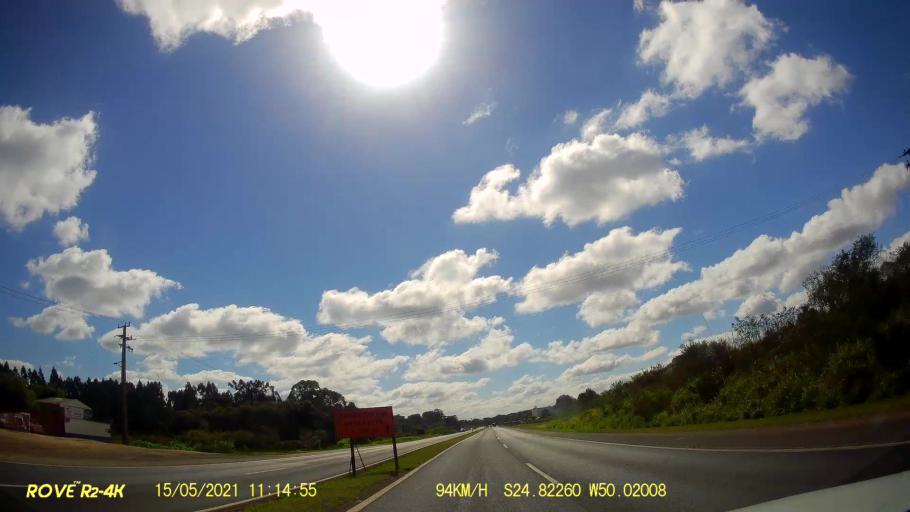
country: BR
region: Parana
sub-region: Castro
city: Castro
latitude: -24.8228
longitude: -50.0202
